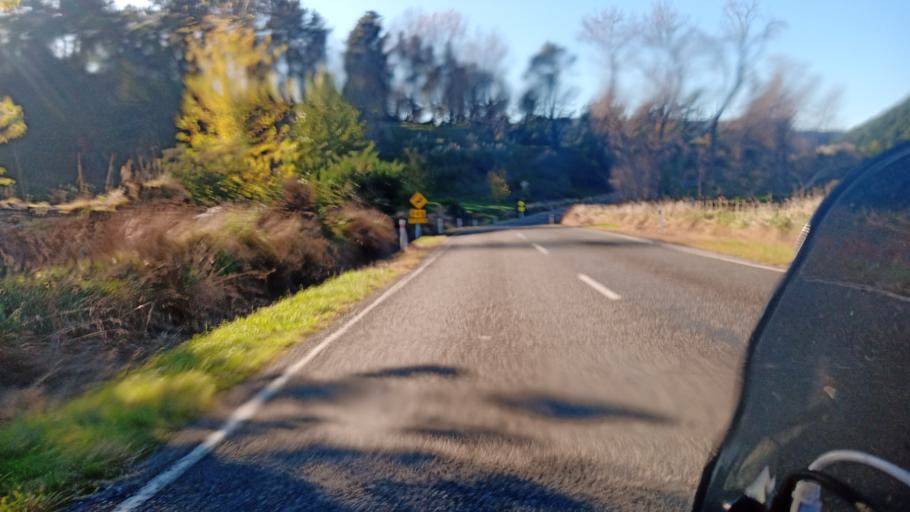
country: NZ
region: Hawke's Bay
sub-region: Wairoa District
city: Wairoa
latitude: -38.8785
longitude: 177.2332
